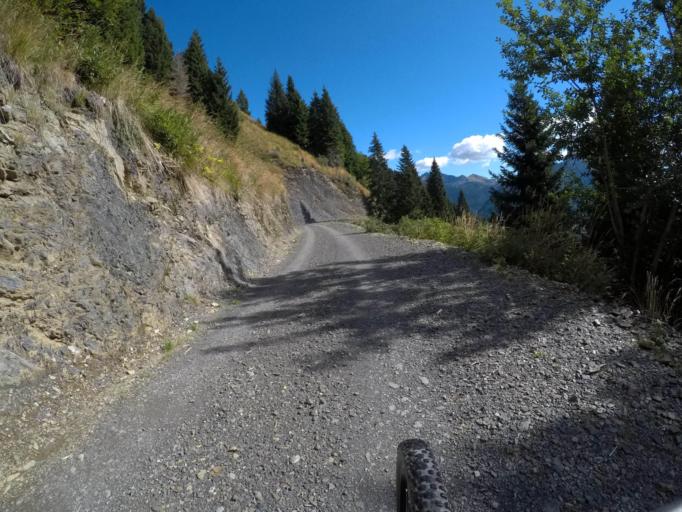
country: IT
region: Friuli Venezia Giulia
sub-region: Provincia di Udine
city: Ligosullo
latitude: 46.5667
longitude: 13.0864
